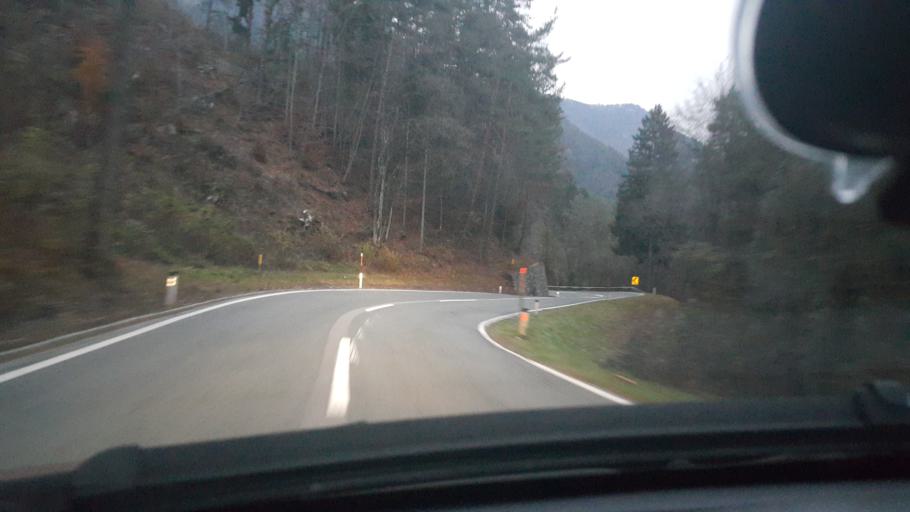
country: AT
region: Carinthia
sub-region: Politischer Bezirk Wolfsberg
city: Sankt Paul im Levanttal
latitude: 46.6686
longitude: 14.8412
